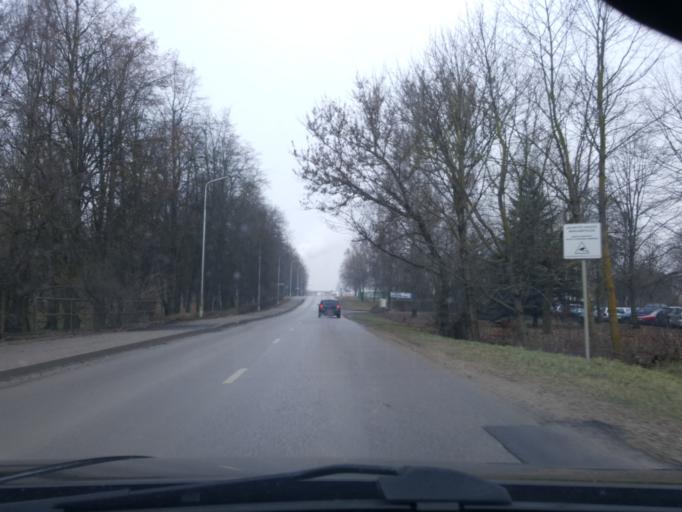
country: LT
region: Marijampoles apskritis
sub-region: Marijampole Municipality
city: Marijampole
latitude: 54.5309
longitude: 23.3540
